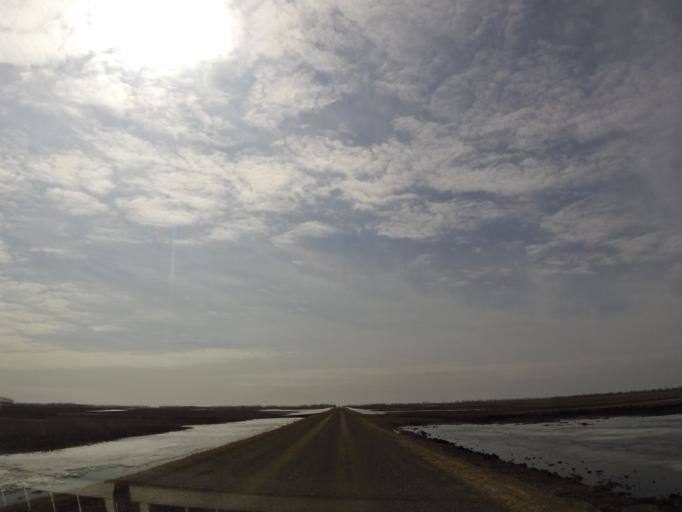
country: US
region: North Dakota
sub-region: Walsh County
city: Grafton
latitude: 48.3471
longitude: -97.2111
